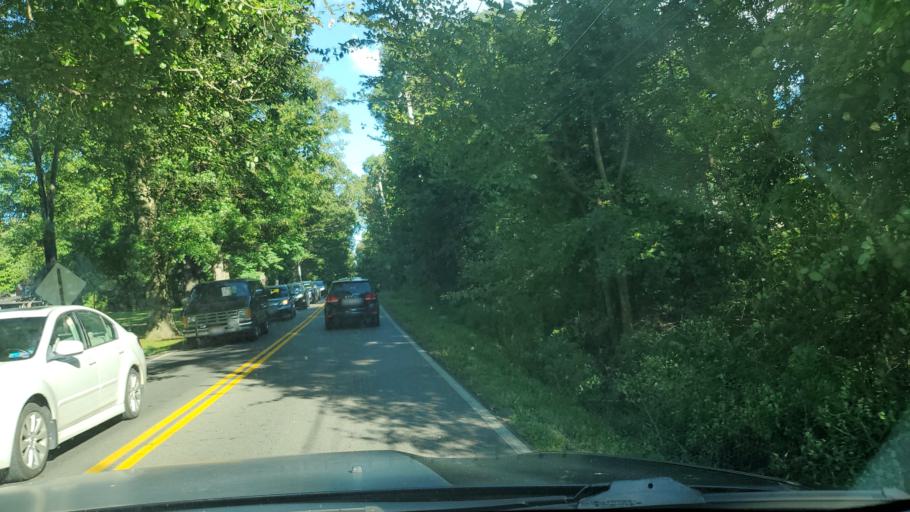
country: US
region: Ohio
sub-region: Mahoning County
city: Boardman
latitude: 41.0467
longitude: -80.6969
